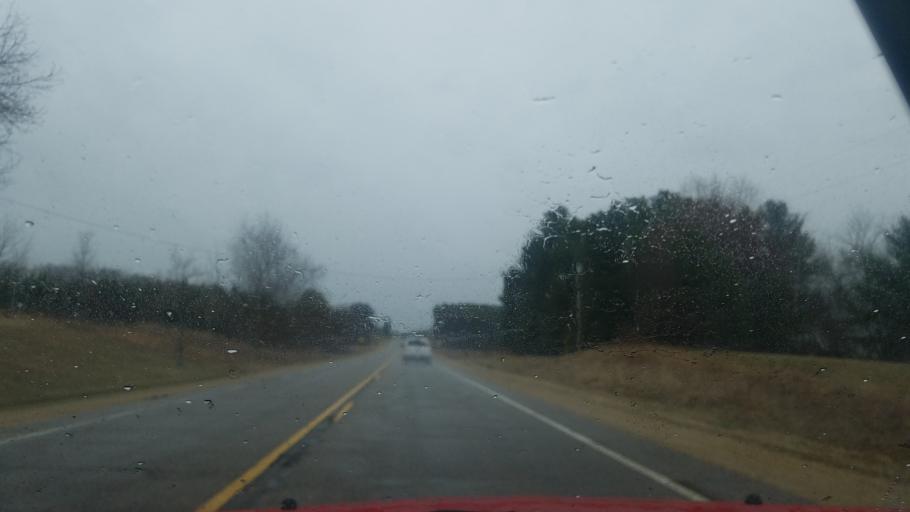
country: US
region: Wisconsin
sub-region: Dunn County
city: Tainter Lake
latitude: 45.0226
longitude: -91.8907
